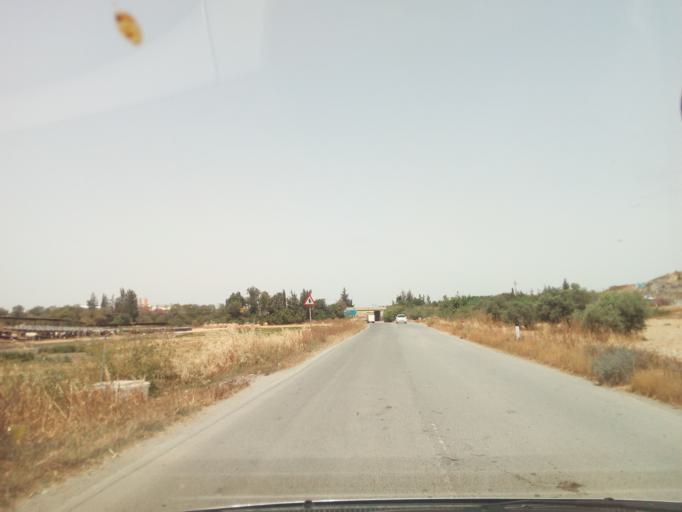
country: CY
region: Larnaka
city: Aradippou
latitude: 34.9596
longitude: 33.5847
